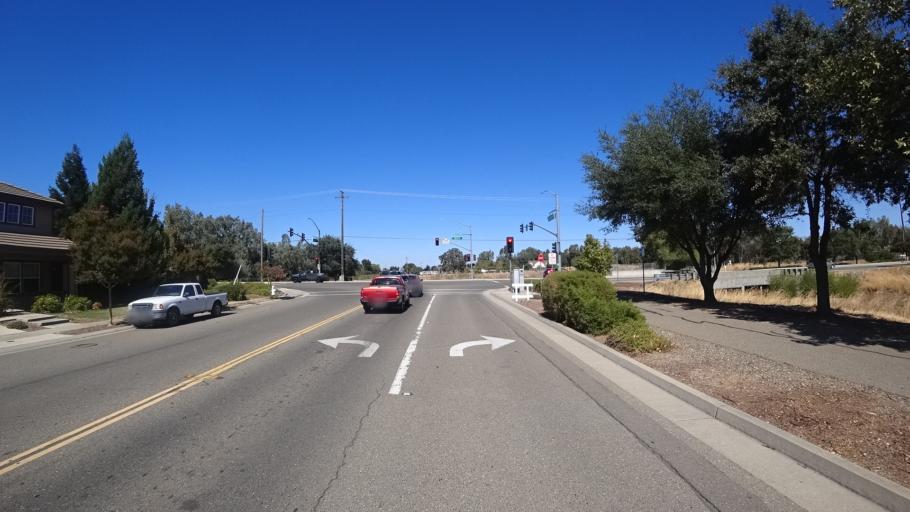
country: US
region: California
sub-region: Sacramento County
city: Elk Grove
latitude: 38.4232
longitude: -121.3480
